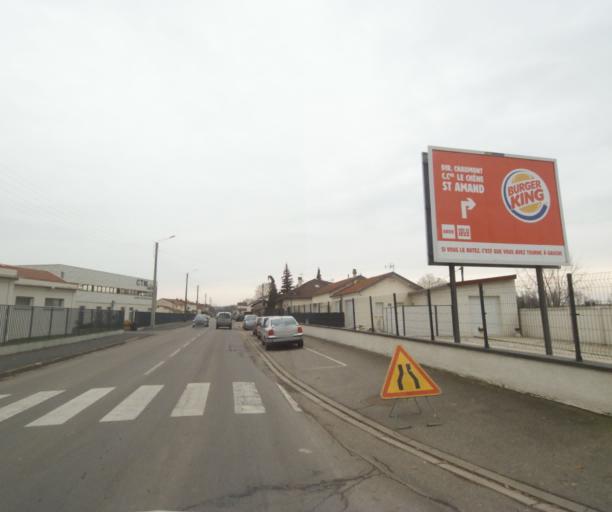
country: FR
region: Champagne-Ardenne
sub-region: Departement de la Haute-Marne
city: Saint-Dizier
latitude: 48.6267
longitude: 4.9479
